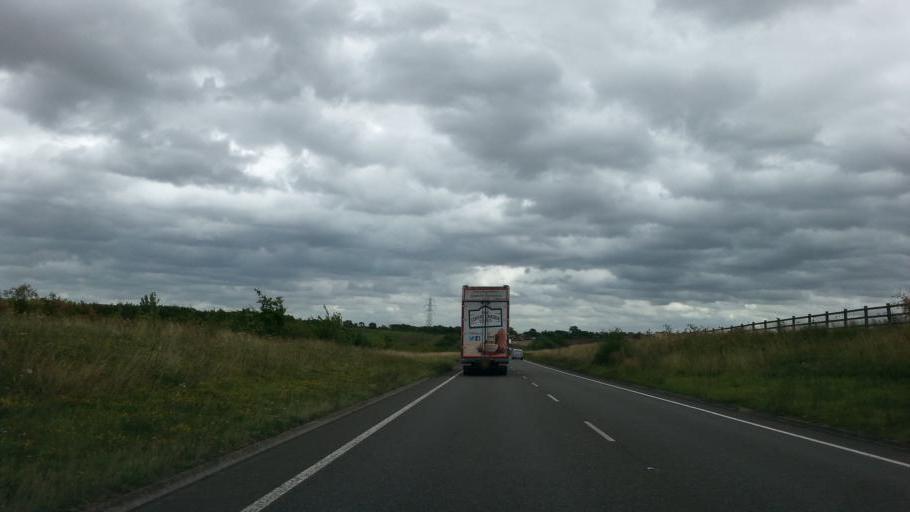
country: GB
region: England
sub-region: Cambridgeshire
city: Papworth Everard
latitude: 52.2430
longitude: -0.1243
